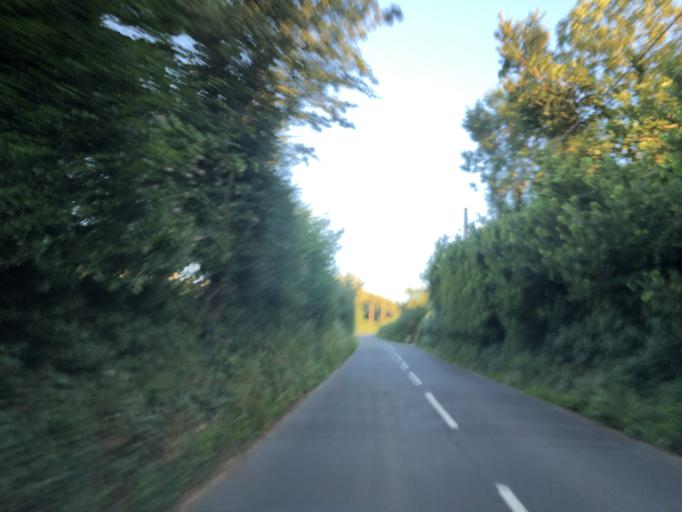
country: GB
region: England
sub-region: Isle of Wight
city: Chale
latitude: 50.5995
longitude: -1.3175
